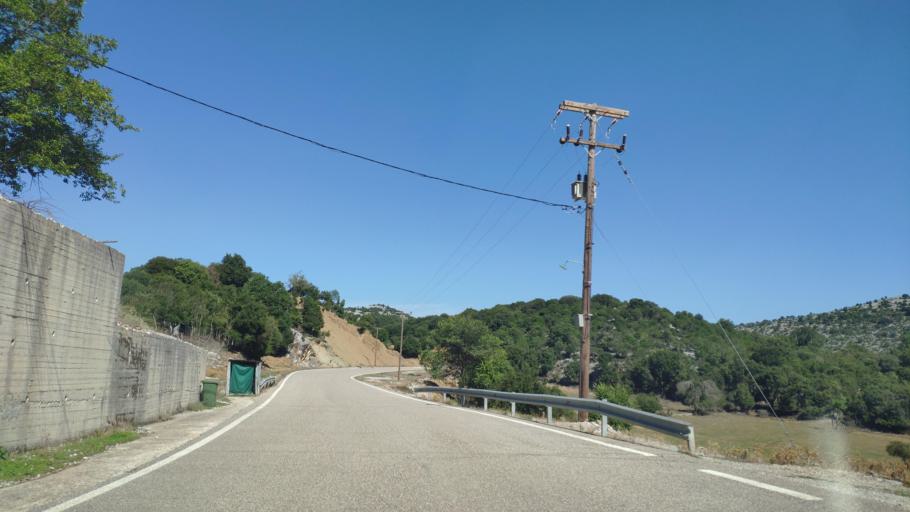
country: GR
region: Central Greece
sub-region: Nomos Evrytanias
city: Kerasochori
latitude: 38.9621
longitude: 21.4631
